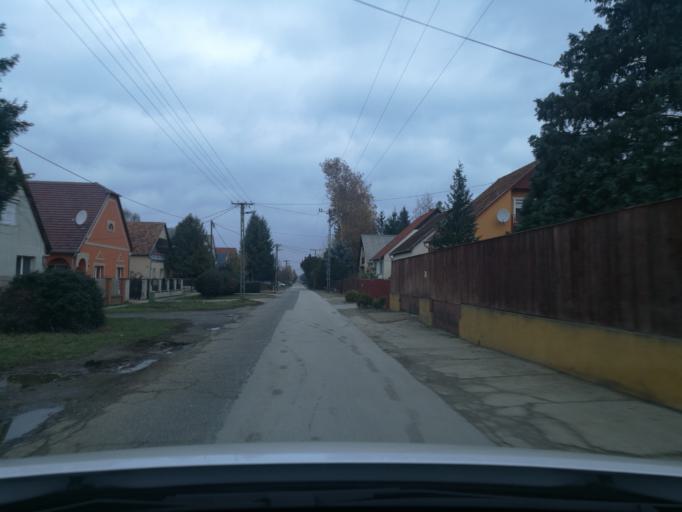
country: HU
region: Szabolcs-Szatmar-Bereg
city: Nyirpazony
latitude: 47.9548
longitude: 21.7763
